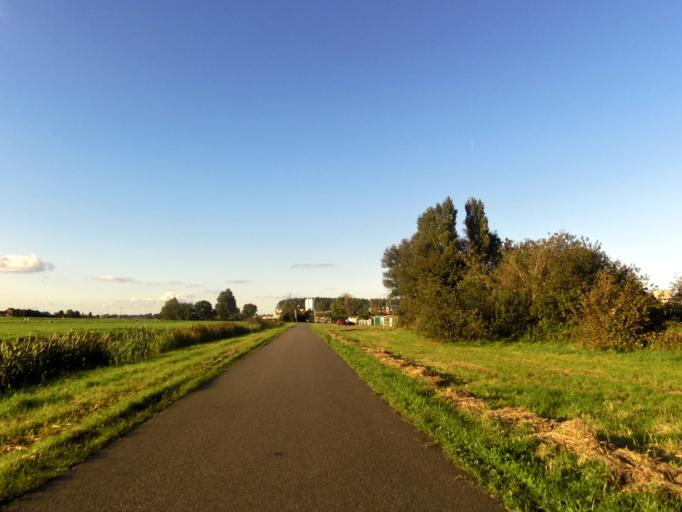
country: NL
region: South Holland
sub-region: Gemeente Alphen aan den Rijn
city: Alphen aan den Rijn
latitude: 52.1456
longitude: 4.6448
